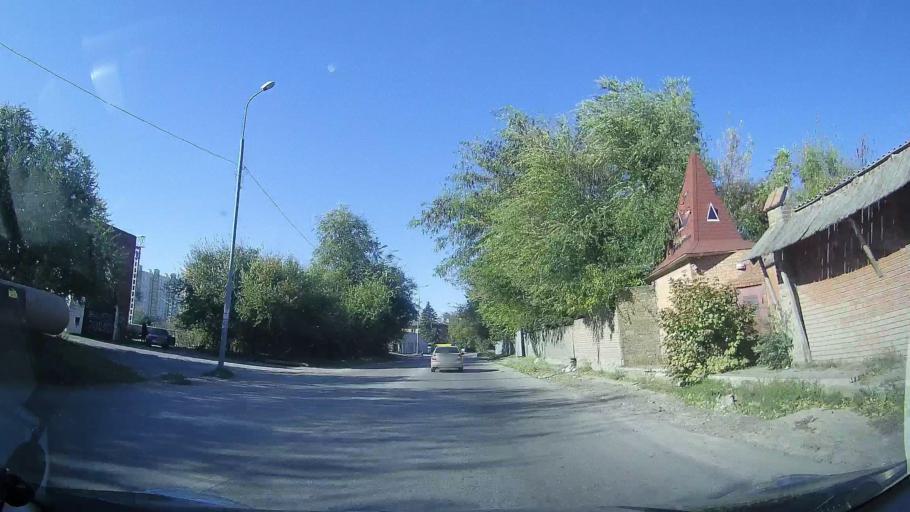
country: RU
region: Rostov
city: Rostov-na-Donu
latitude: 47.2265
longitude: 39.6736
